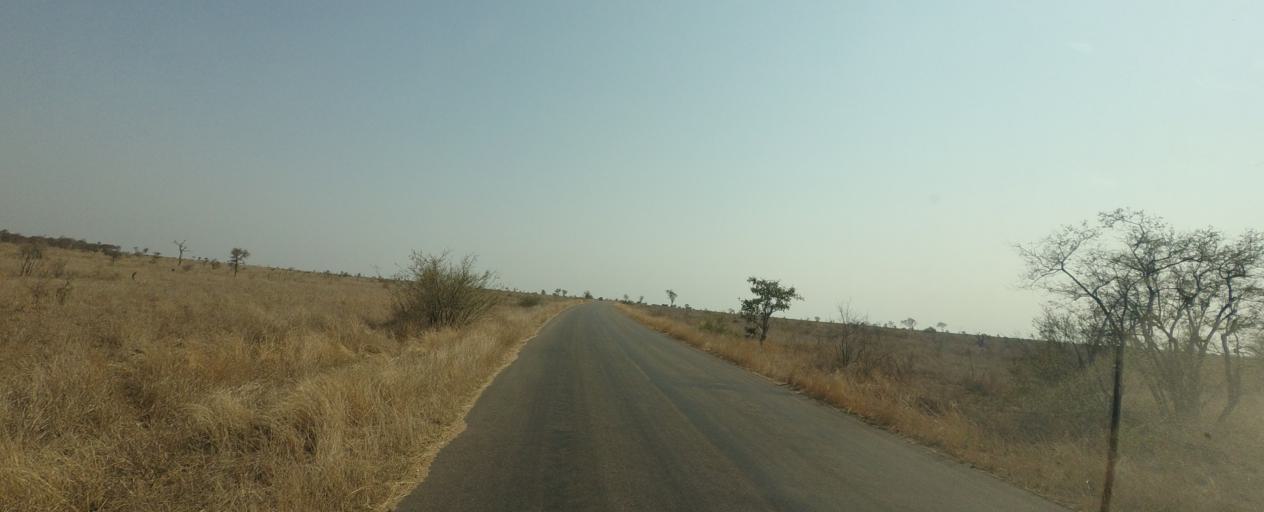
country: ZA
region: Limpopo
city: Thulamahashi
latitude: -24.3603
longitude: 31.7636
